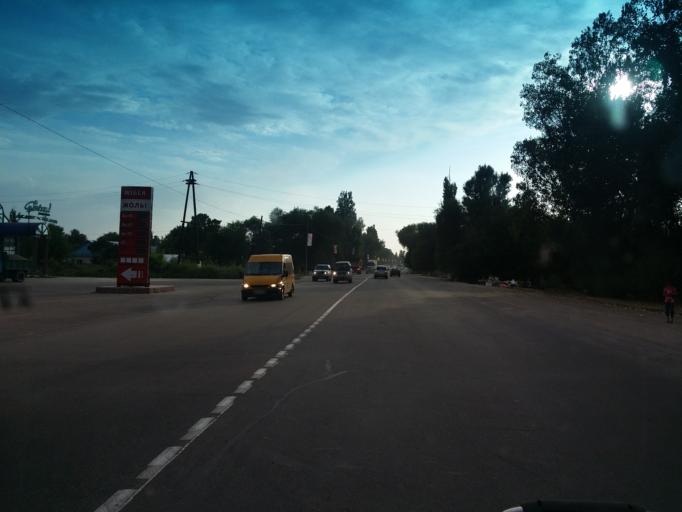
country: KZ
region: Almaty Oblysy
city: Talghar
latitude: 43.4062
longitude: 77.2340
